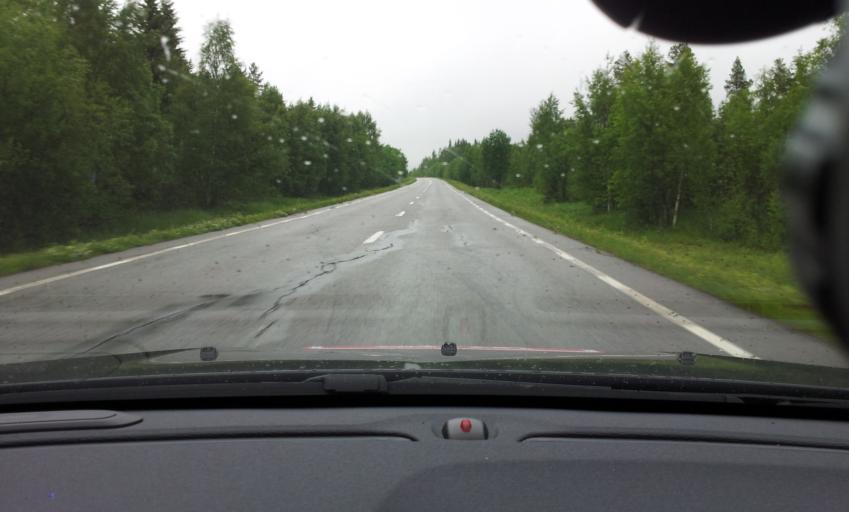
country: SE
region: Jaemtland
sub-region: Krokoms Kommun
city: Krokom
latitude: 63.4968
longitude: 14.5098
